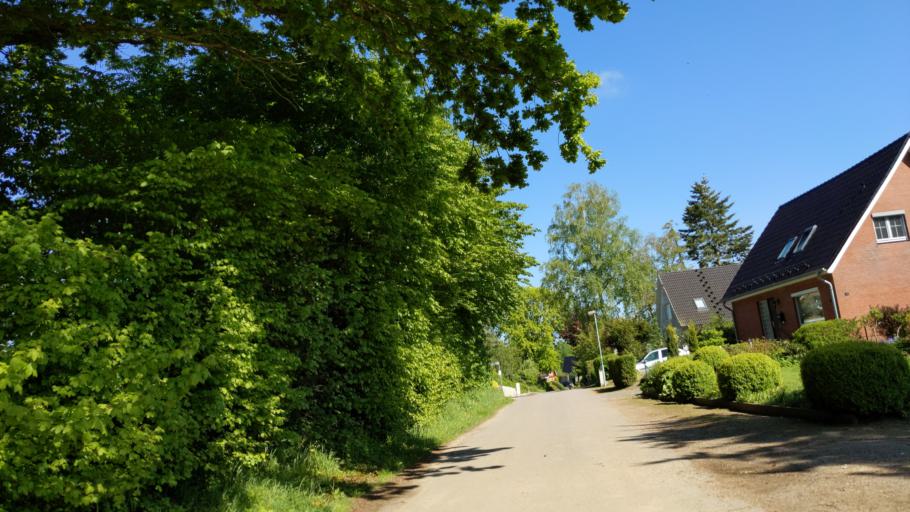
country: DE
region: Schleswig-Holstein
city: Eutin
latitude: 54.0957
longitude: 10.6096
